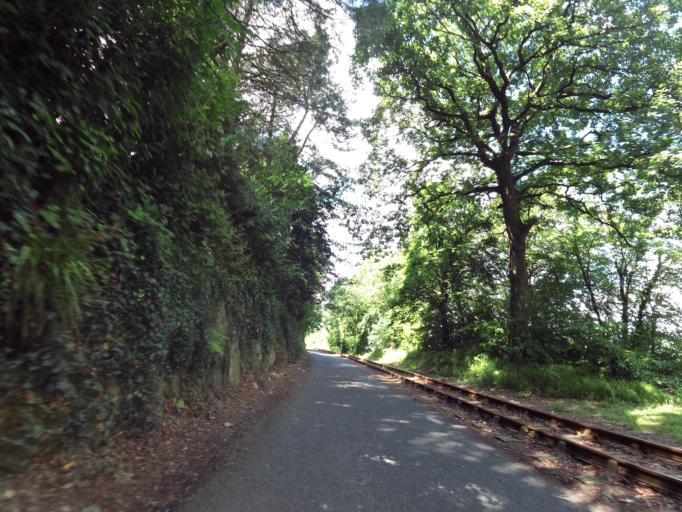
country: IE
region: Leinster
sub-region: Kilkenny
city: Mooncoin
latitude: 52.2450
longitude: -7.2269
